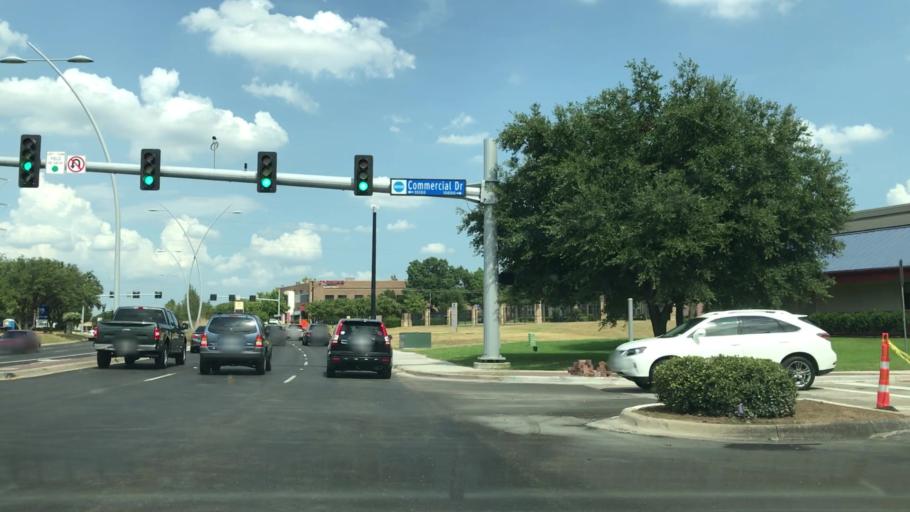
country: US
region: Texas
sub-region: Dallas County
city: Addison
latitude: 32.9531
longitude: -96.8496
